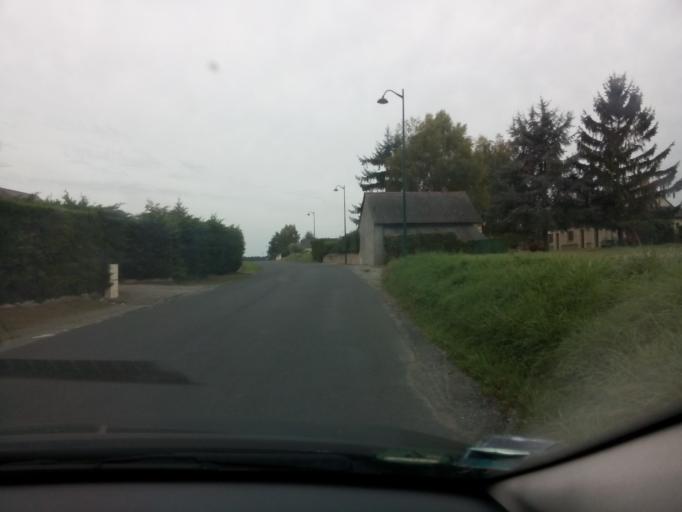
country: FR
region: Pays de la Loire
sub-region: Departement de Maine-et-Loire
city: Baune
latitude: 47.4994
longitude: -0.3222
